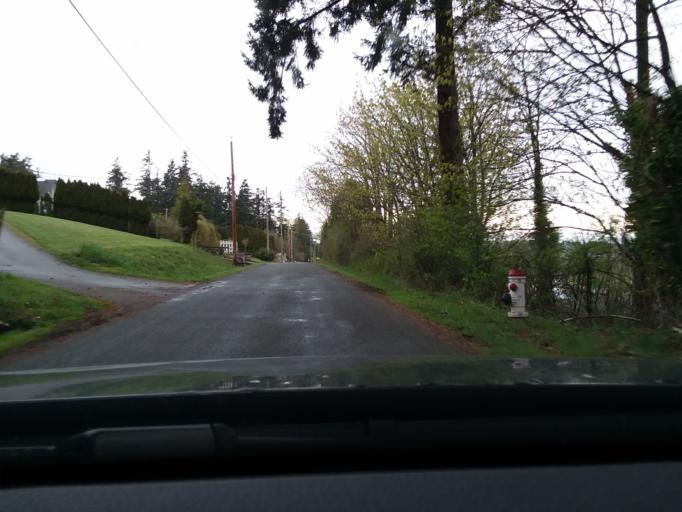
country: CA
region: British Columbia
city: North Saanich
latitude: 48.5515
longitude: -123.3900
